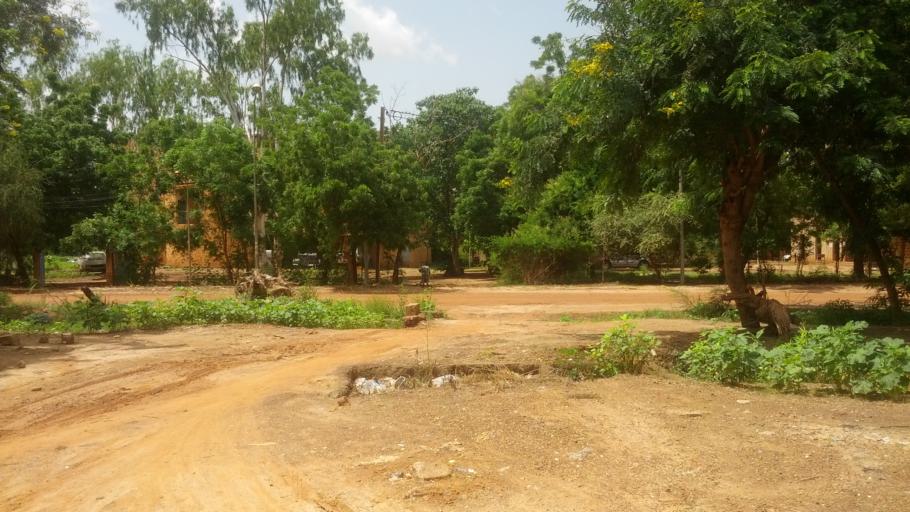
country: BF
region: Centre
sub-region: Kadiogo Province
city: Ouagadougou
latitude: 12.3777
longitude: -1.5029
